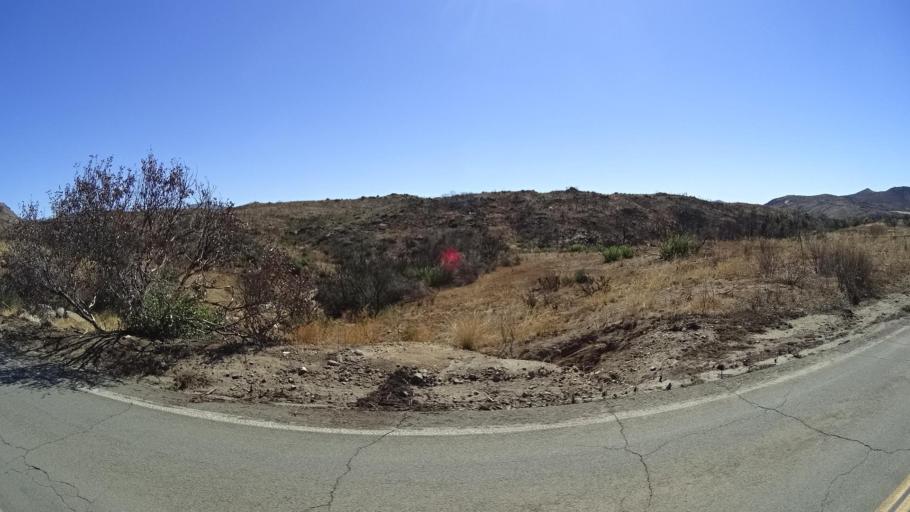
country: US
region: California
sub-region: San Diego County
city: Alpine
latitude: 32.7313
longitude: -116.6944
